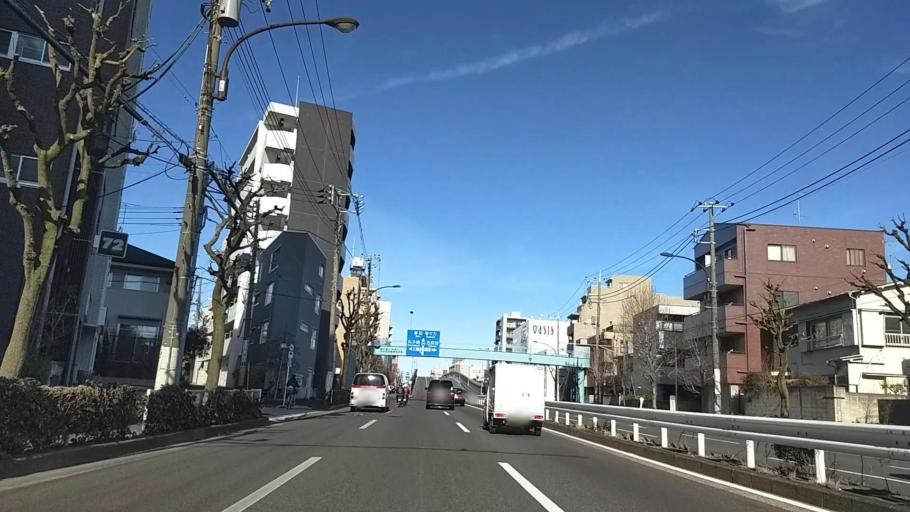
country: JP
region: Kanagawa
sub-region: Kawasaki-shi
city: Kawasaki
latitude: 35.5862
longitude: 139.6795
